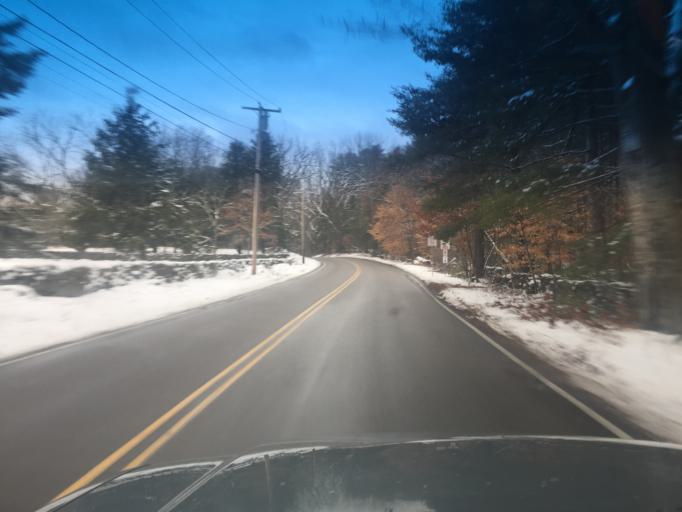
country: US
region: Massachusetts
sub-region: Norfolk County
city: Millis
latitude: 42.1931
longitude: -71.3852
